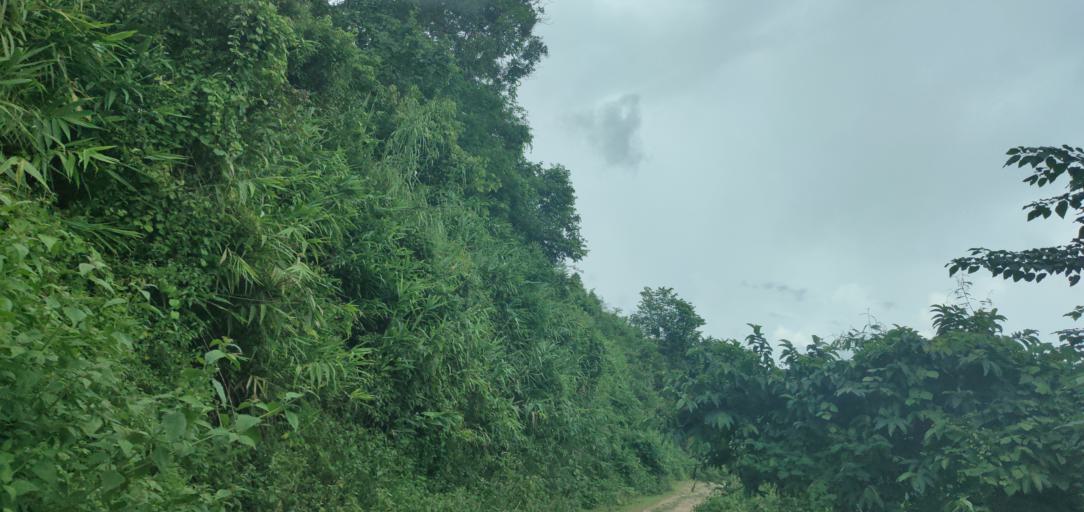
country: LA
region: Phongsali
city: Phongsali
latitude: 21.4418
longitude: 102.3260
